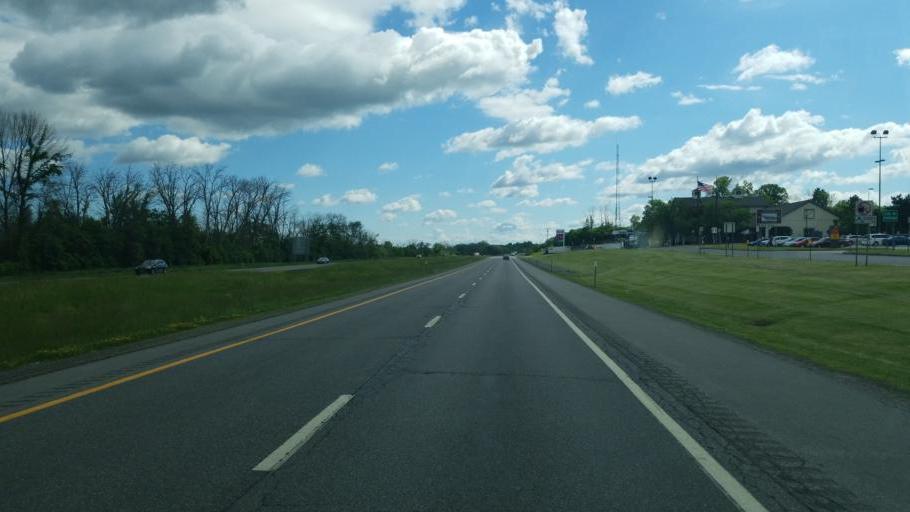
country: US
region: New York
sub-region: Cayuga County
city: Port Byron
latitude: 43.0235
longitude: -76.6729
